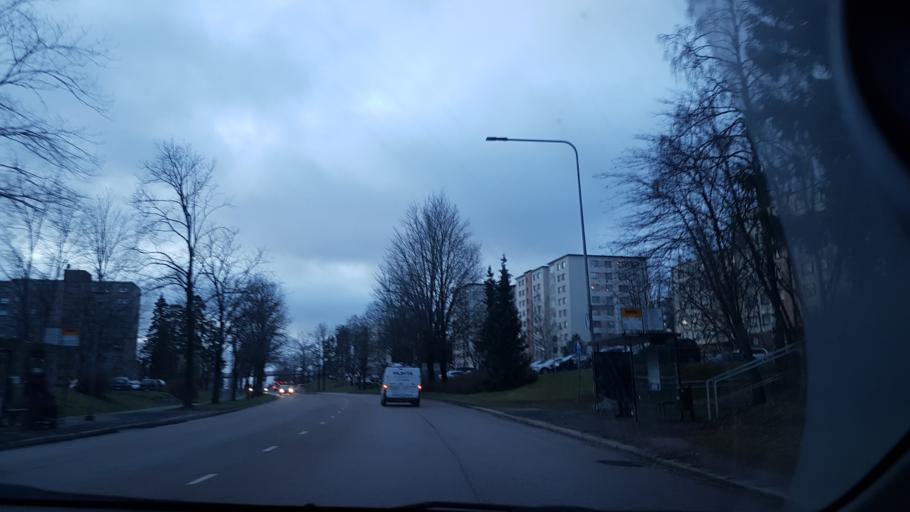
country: FI
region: Uusimaa
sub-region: Helsinki
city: Vantaa
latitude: 60.2765
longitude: 25.1045
